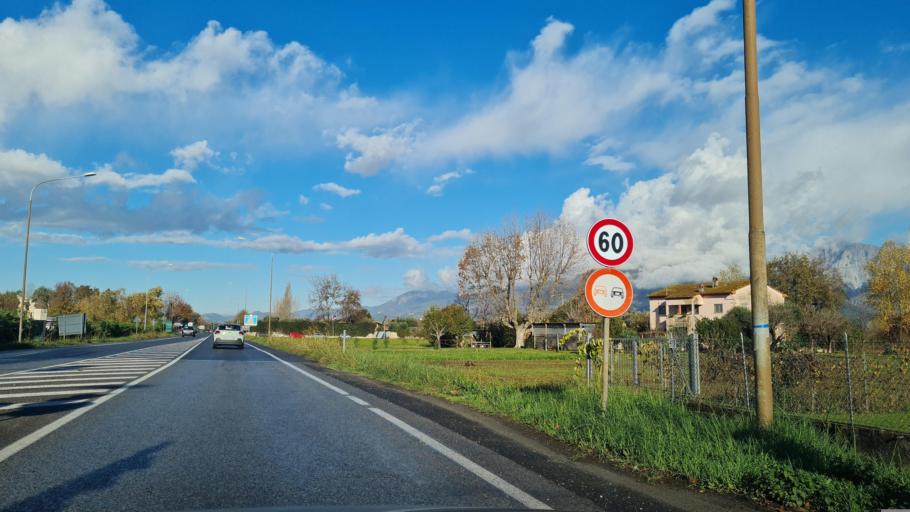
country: IT
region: Tuscany
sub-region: Provincia di Lucca
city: Pietrasanta
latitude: 43.9465
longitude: 10.2068
